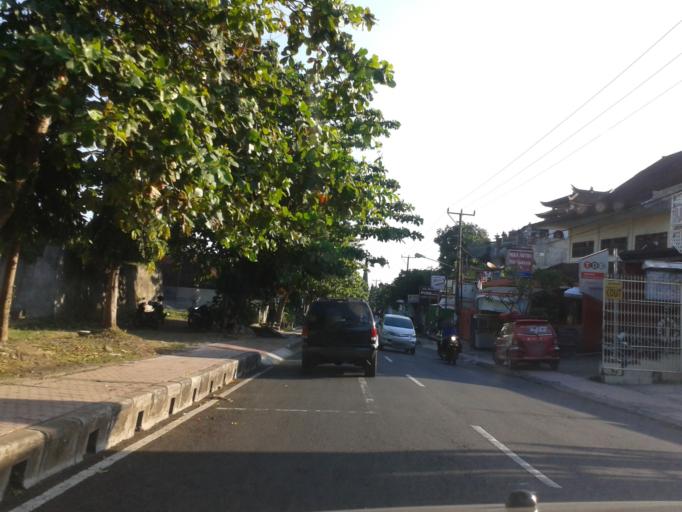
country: ID
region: Bali
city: Semarapura
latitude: -8.5314
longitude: 115.4045
